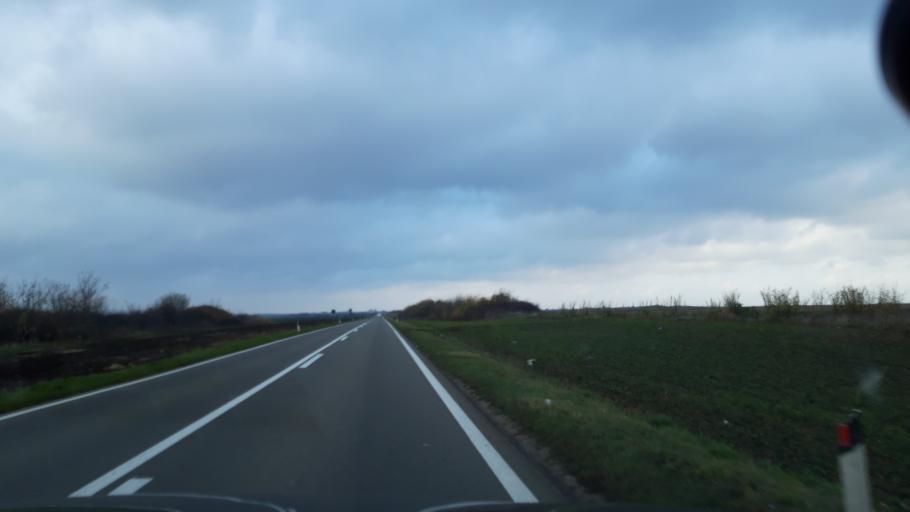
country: RS
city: Sanad
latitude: 46.0004
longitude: 20.1026
